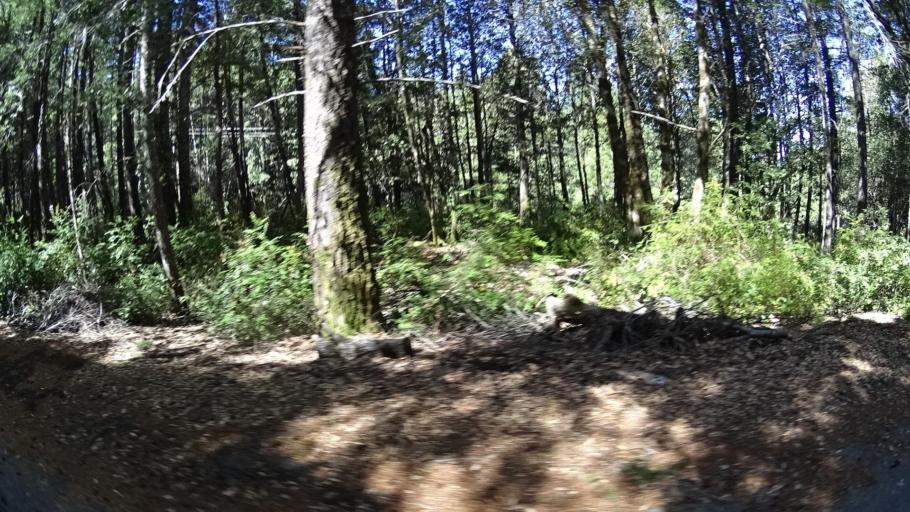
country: US
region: California
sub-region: Humboldt County
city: Redway
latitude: 40.2038
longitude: -124.1031
